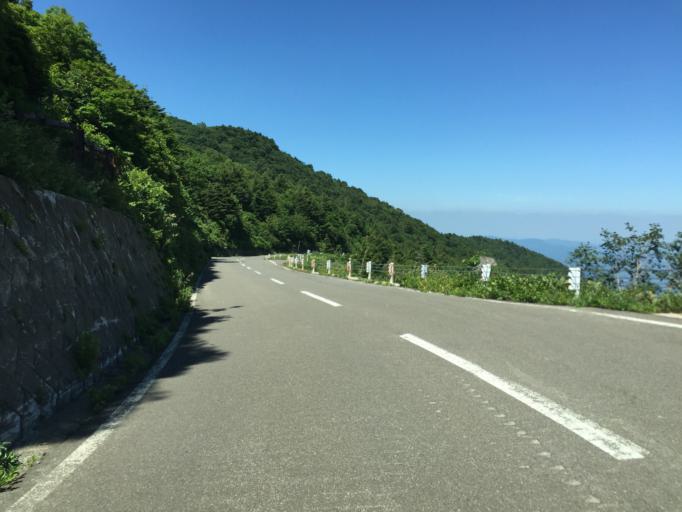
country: JP
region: Fukushima
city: Fukushima-shi
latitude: 37.7380
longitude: 140.2682
